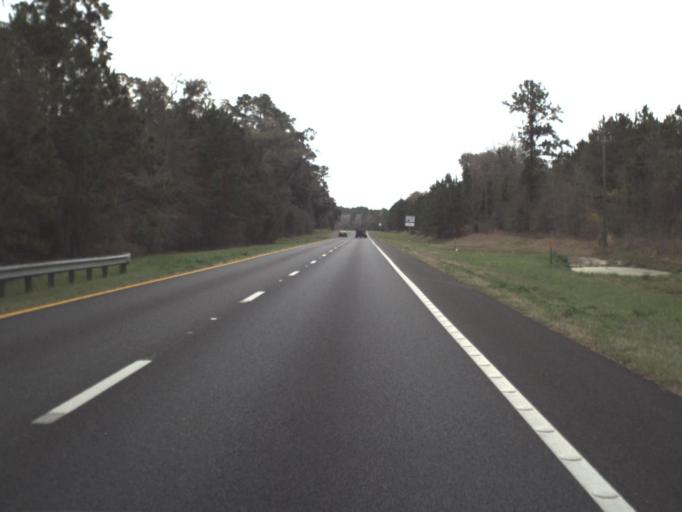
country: US
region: Florida
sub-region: Leon County
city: Tallahassee
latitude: 30.6395
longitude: -84.1685
